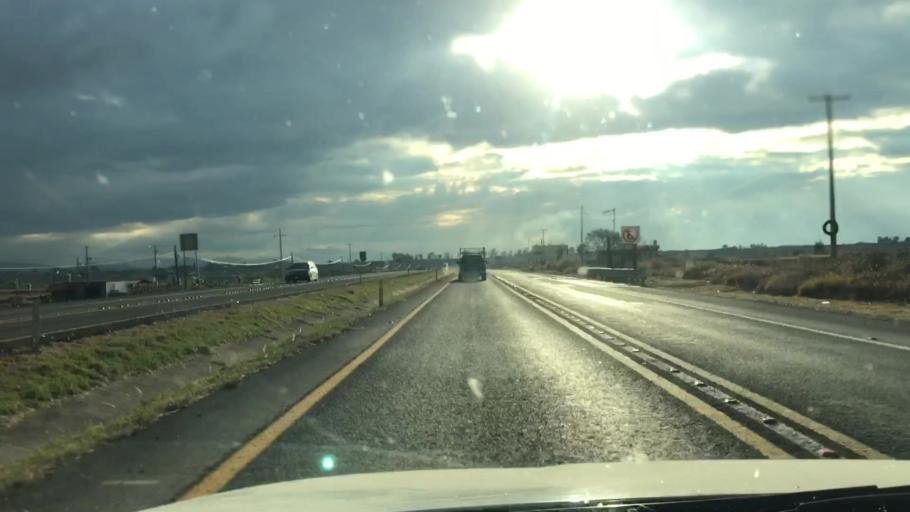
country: MX
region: Guanajuato
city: Penjamo
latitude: 20.3954
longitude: -101.7568
